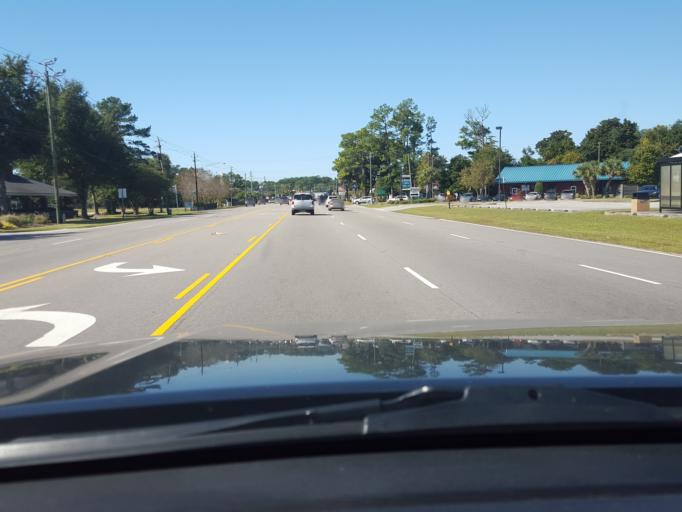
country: US
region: North Carolina
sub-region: New Hanover County
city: Seagate
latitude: 34.2083
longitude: -77.8595
